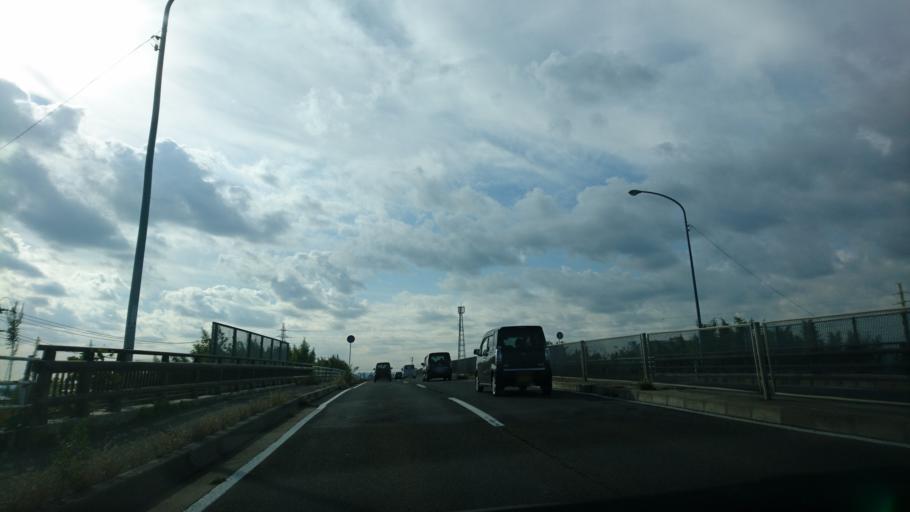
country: JP
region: Miyagi
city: Furukawa
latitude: 38.5722
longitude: 140.9468
